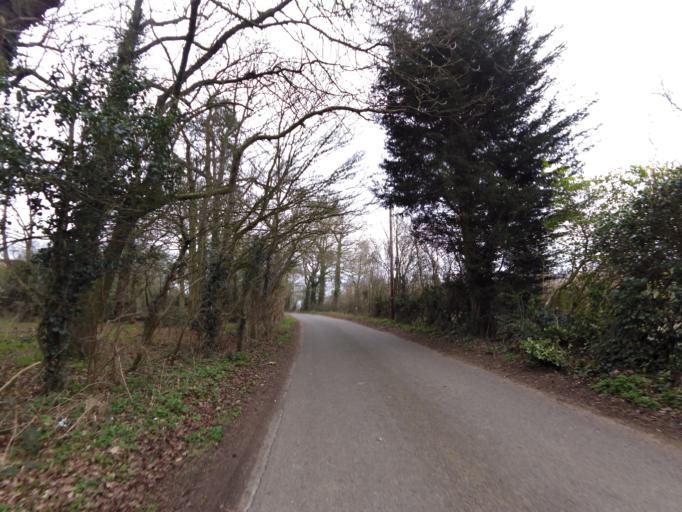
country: GB
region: England
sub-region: Suffolk
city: Halesworth
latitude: 52.3497
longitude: 1.5259
